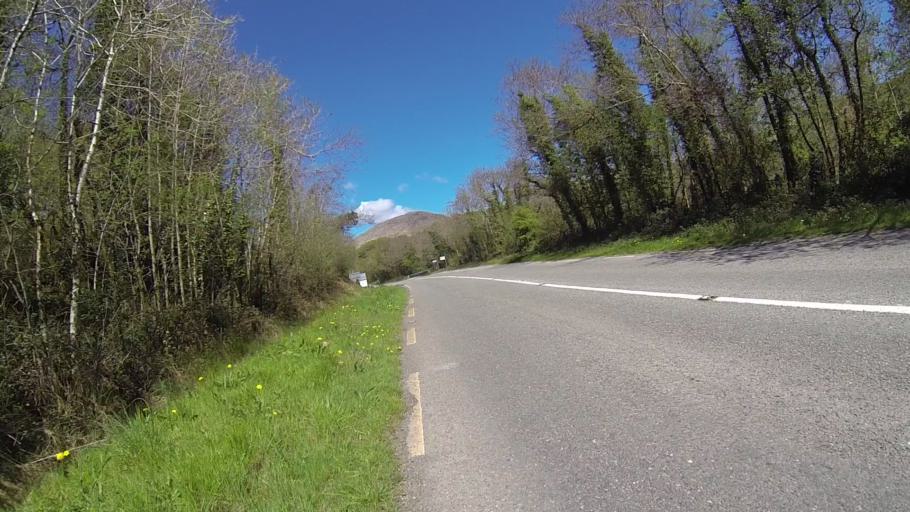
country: IE
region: Munster
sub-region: Ciarrai
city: Kenmare
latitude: 51.9013
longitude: -9.5986
